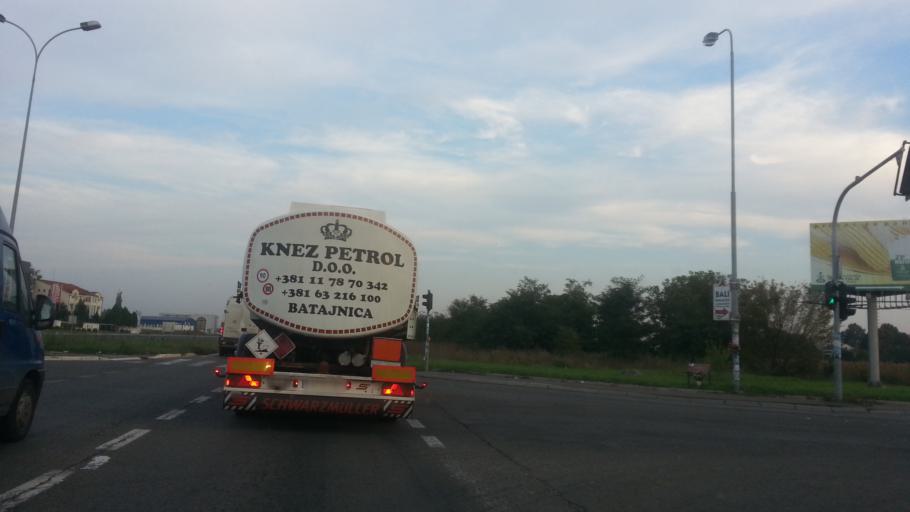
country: RS
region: Central Serbia
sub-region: Belgrade
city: Zemun
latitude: 44.8721
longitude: 20.3340
